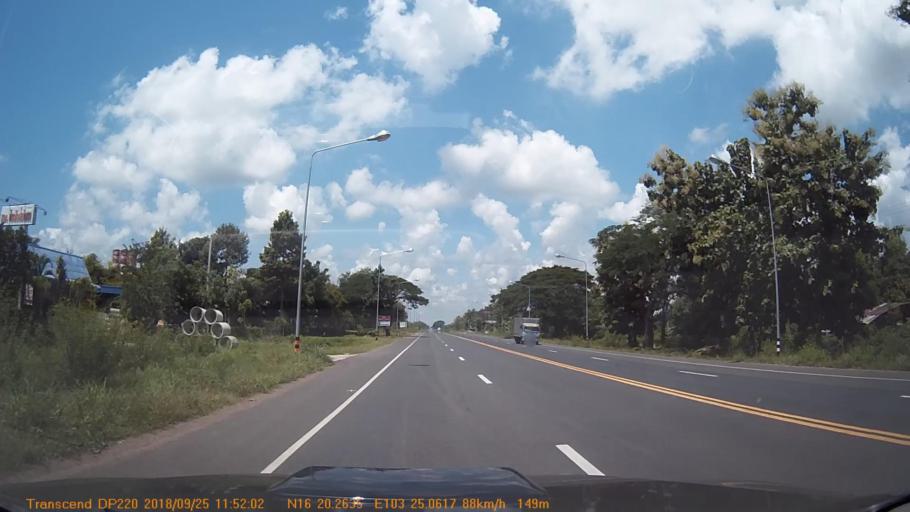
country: TH
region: Kalasin
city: Yang Talat
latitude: 16.3378
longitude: 103.4176
